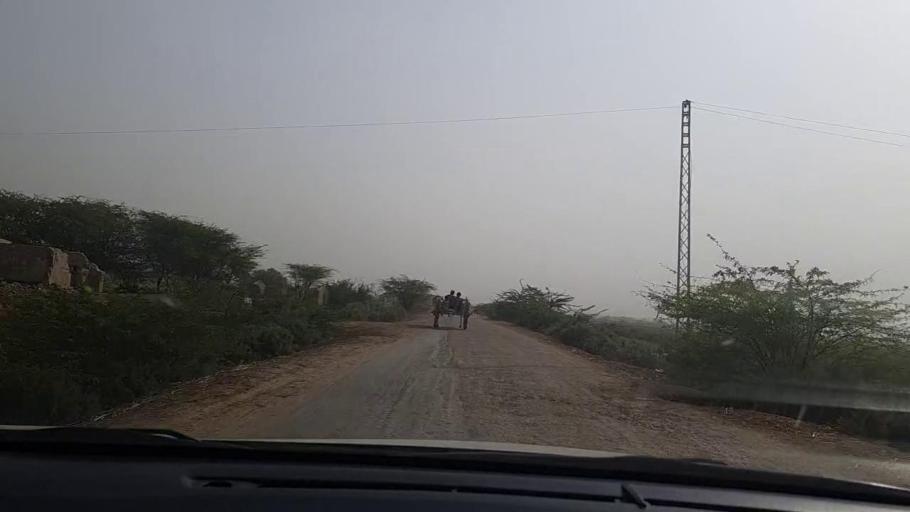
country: PK
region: Sindh
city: Pithoro
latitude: 25.4220
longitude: 69.3159
